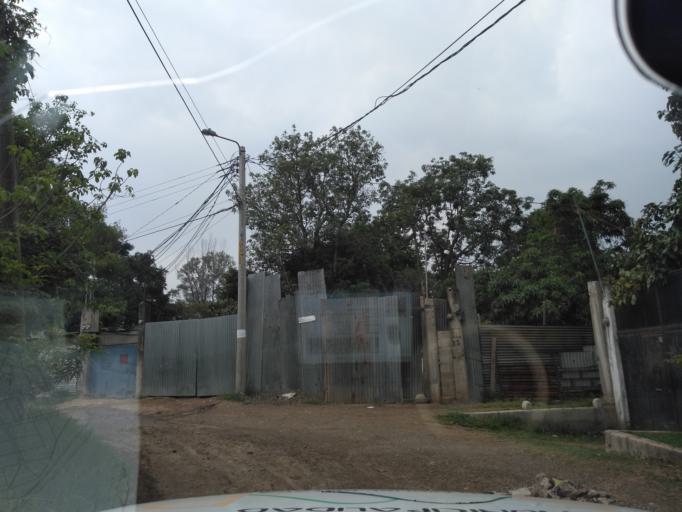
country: GT
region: Guatemala
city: Petapa
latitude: 14.5101
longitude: -90.5554
